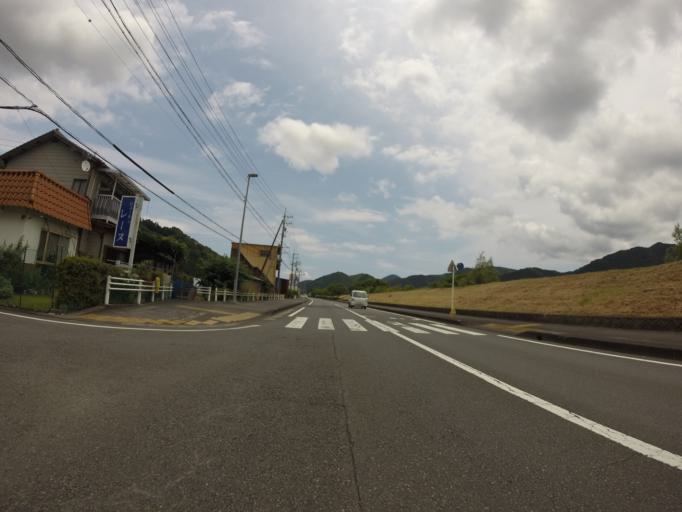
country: JP
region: Shizuoka
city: Shizuoka-shi
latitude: 34.9865
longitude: 138.3070
